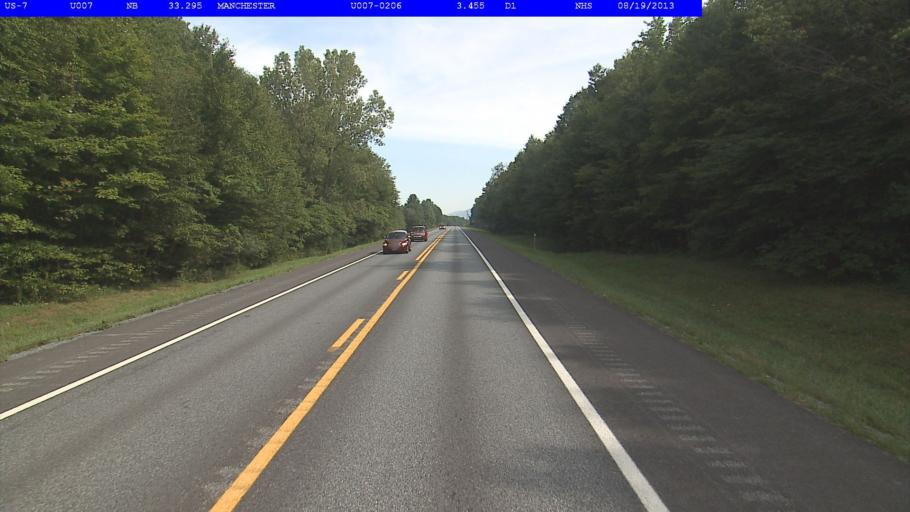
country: US
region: Vermont
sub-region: Bennington County
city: Manchester Center
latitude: 43.1590
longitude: -73.0430
